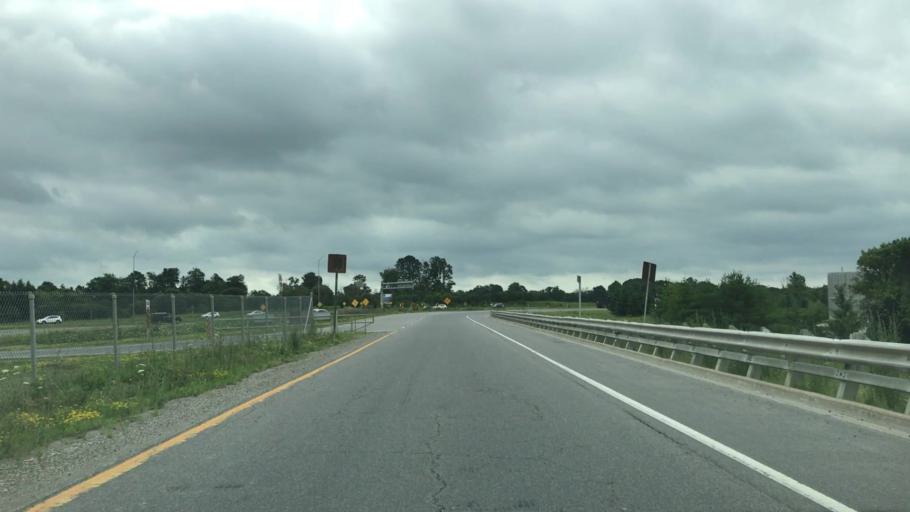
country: CA
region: Ontario
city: Newmarket
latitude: 44.0121
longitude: -79.4081
